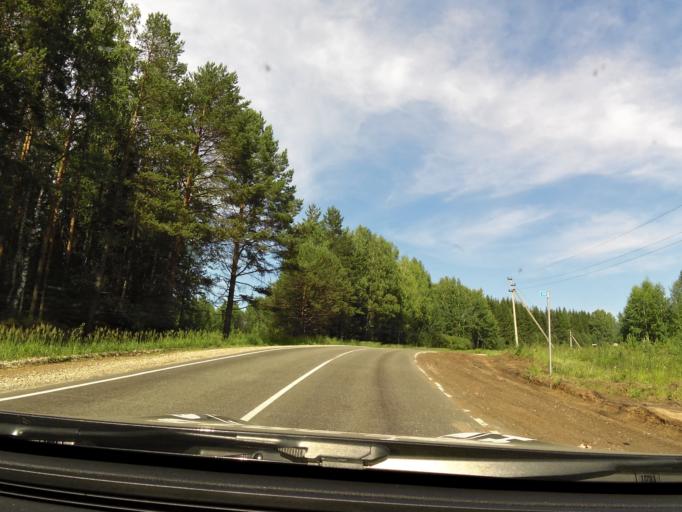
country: RU
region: Kirov
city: Belaya Kholunitsa
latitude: 58.8414
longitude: 50.6893
